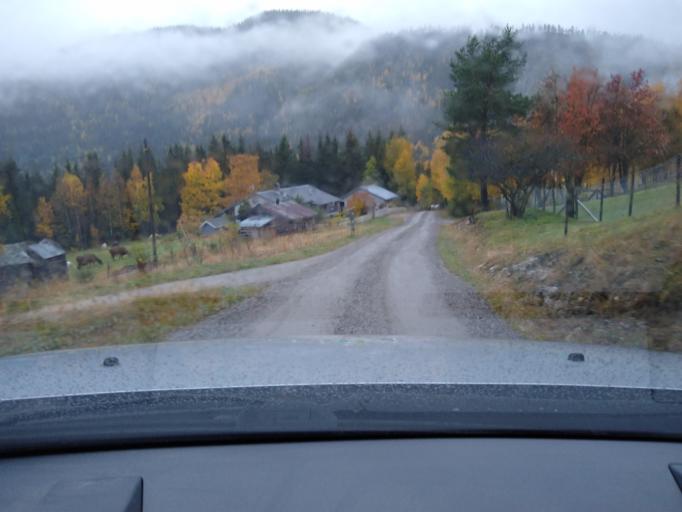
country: NO
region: Oppland
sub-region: Ringebu
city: Ringebu
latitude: 61.5517
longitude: 10.1544
